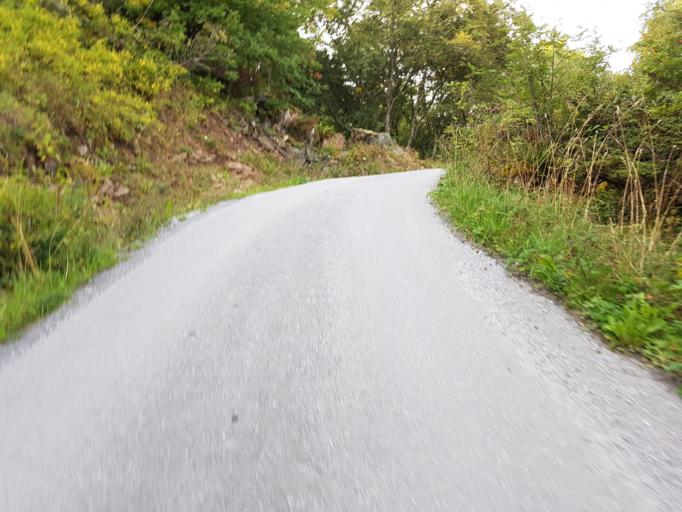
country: NO
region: Sor-Trondelag
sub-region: Afjord
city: A i Afjord
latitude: 64.0557
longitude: 9.9537
